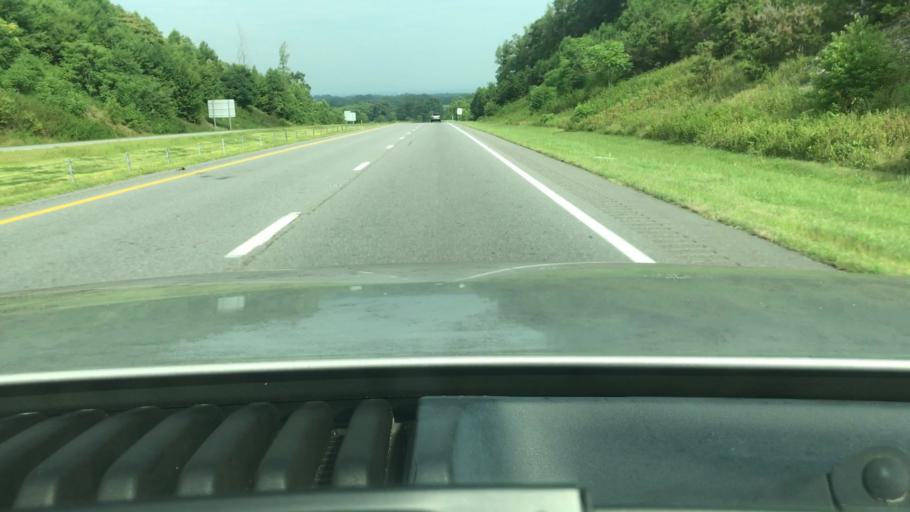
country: US
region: North Carolina
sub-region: Yadkin County
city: Jonesville
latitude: 36.1584
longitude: -80.9394
